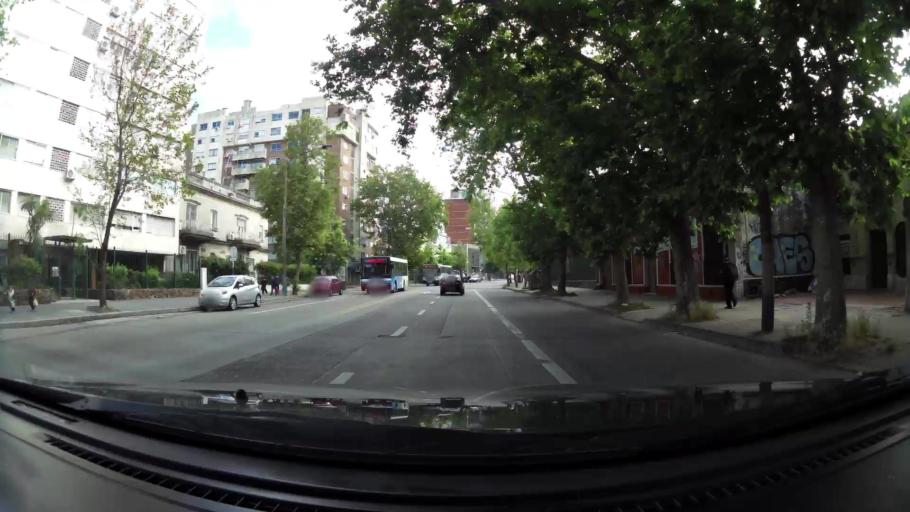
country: UY
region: Montevideo
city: Montevideo
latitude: -34.8844
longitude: -56.1559
